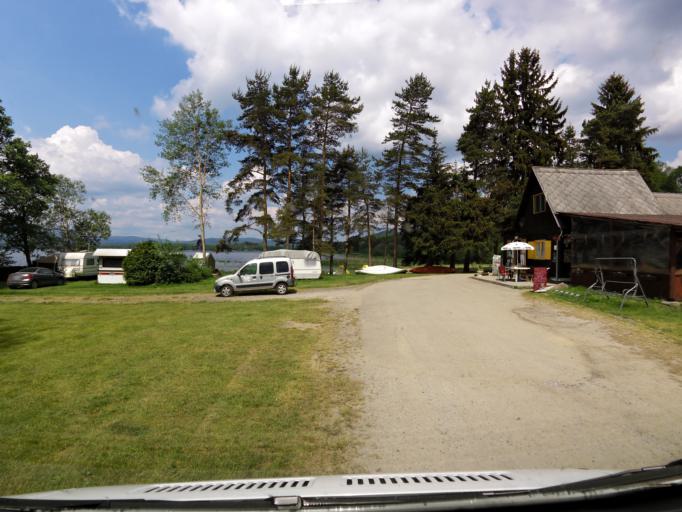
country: CZ
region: Jihocesky
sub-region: Okres Cesky Krumlov
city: Horni Plana
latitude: 48.7741
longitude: 14.0139
